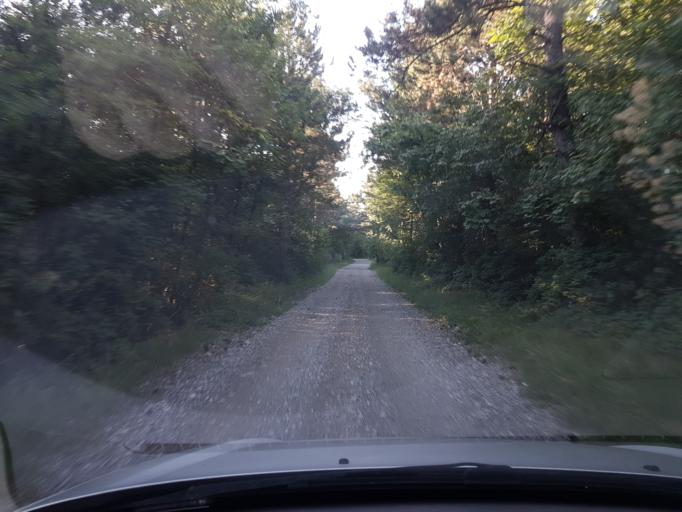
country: SI
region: Sezana
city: Sezana
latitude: 45.7175
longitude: 13.9099
